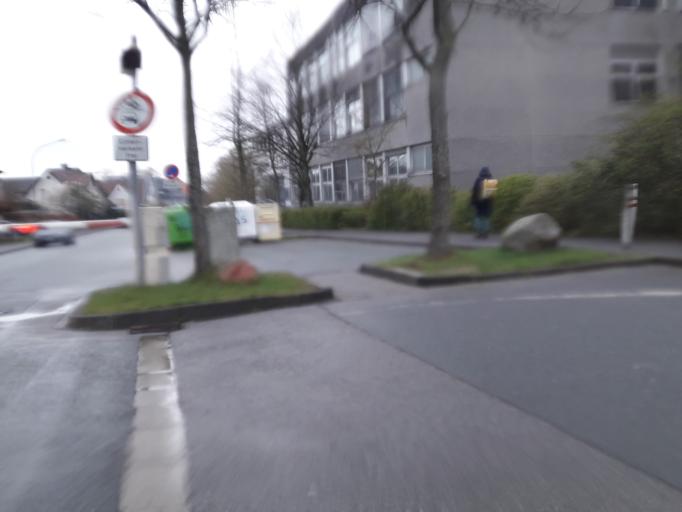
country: DE
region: North Rhine-Westphalia
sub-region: Regierungsbezirk Detmold
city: Paderborn
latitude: 51.7085
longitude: 8.7680
